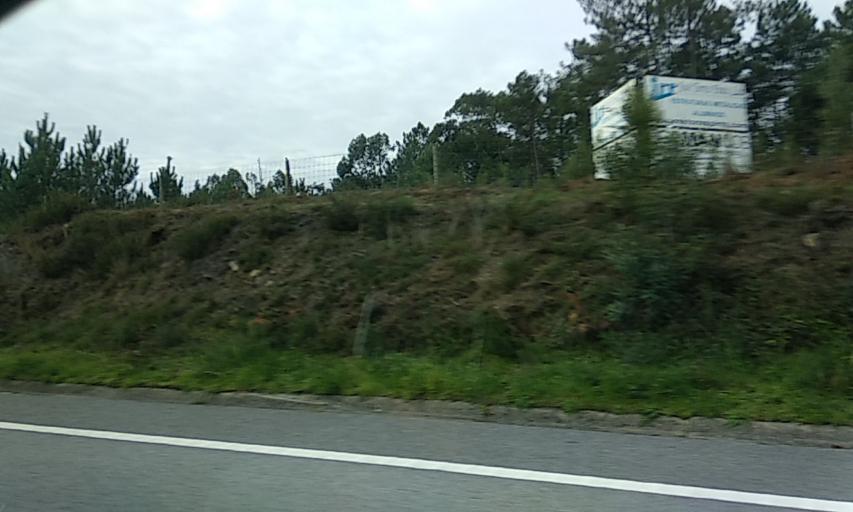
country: PT
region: Porto
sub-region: Santo Tirso
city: Santo Tirso
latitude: 41.3387
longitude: -8.5080
